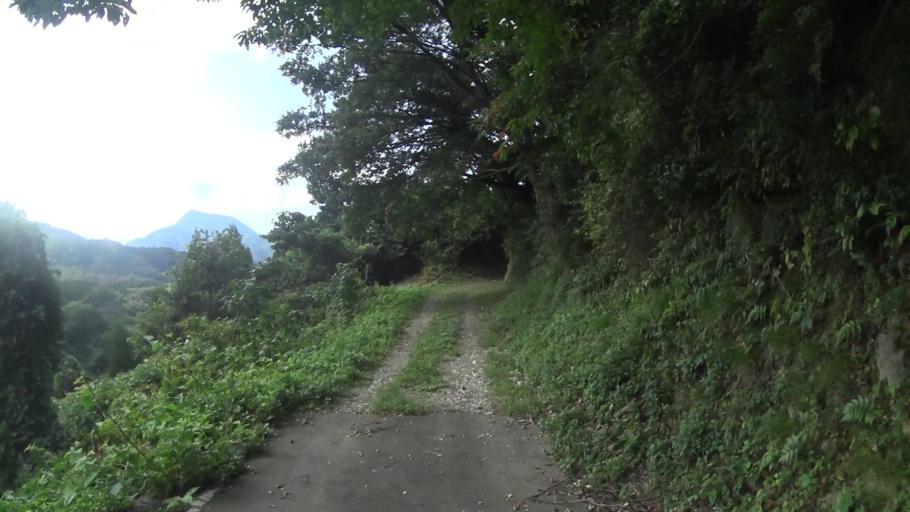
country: JP
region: Kyoto
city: Miyazu
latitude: 35.7419
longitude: 135.1976
